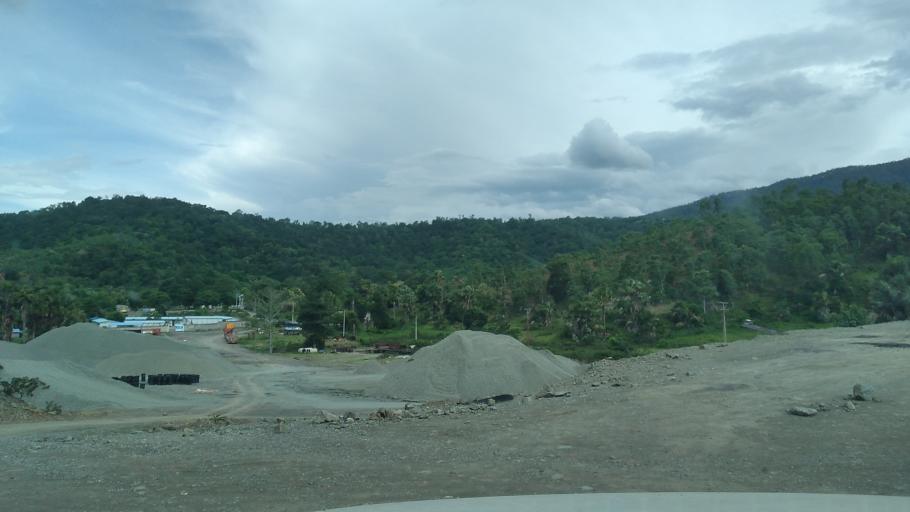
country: TL
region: Dili
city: Dili
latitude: -8.5982
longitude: 125.4773
